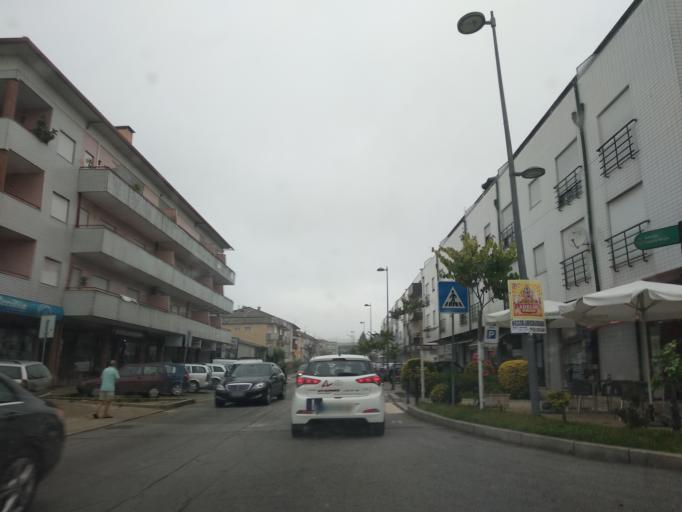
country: PT
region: Braga
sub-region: Vila Verde
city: Vila Verde
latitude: 41.6447
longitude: -8.4355
